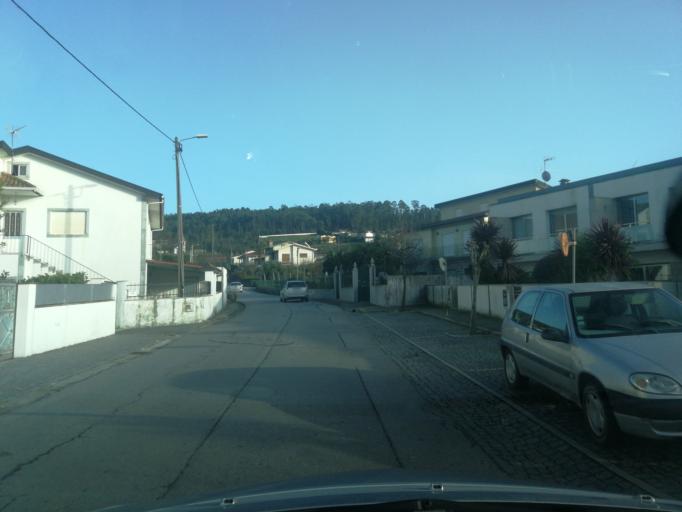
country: PT
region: Braga
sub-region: Barcelos
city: Galegos
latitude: 41.5168
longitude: -8.5653
